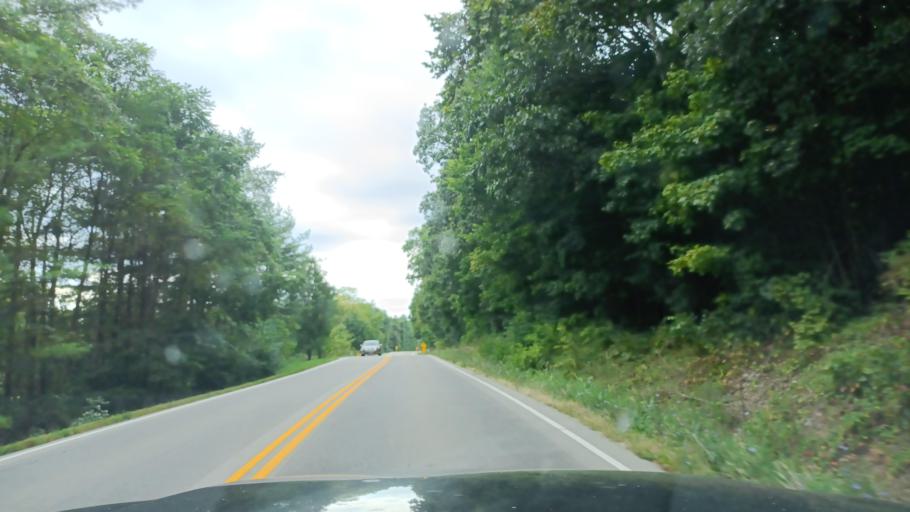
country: US
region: Ohio
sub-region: Ross County
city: Chillicothe
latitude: 39.2836
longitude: -82.8569
